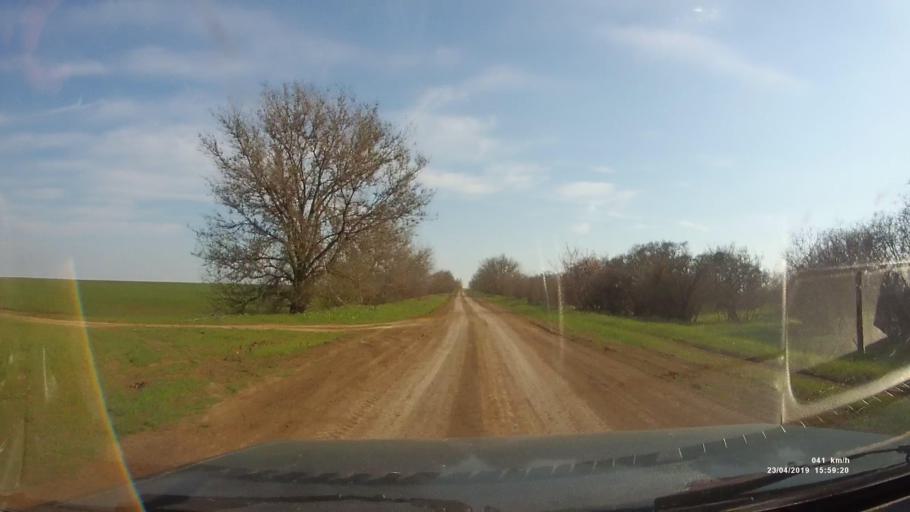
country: RU
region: Rostov
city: Remontnoye
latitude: 46.5176
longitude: 43.1096
